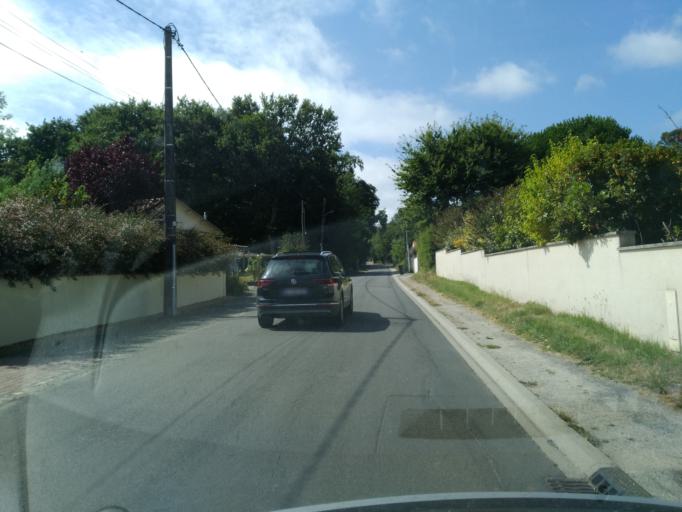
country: FR
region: Poitou-Charentes
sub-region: Departement de la Charente-Maritime
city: Breuillet
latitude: 45.6936
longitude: -1.0694
